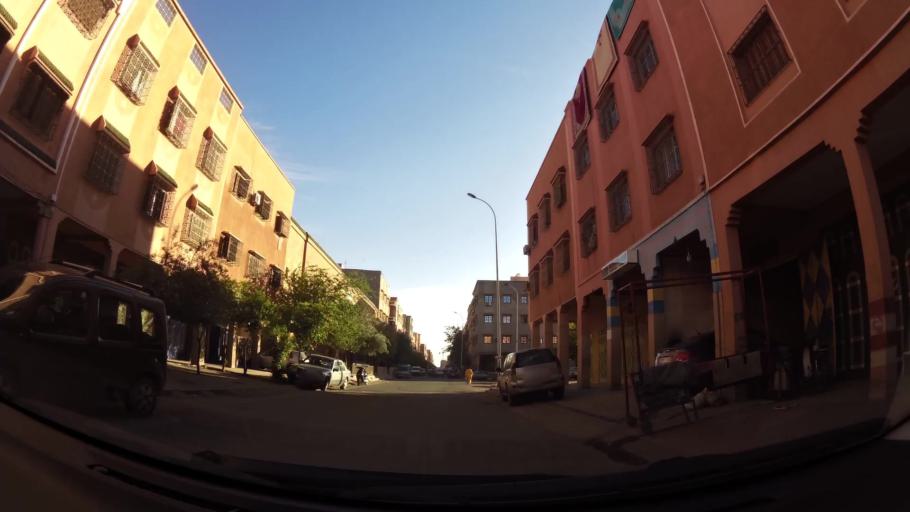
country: MA
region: Marrakech-Tensift-Al Haouz
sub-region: Marrakech
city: Marrakesh
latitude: 31.6187
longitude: -8.0614
